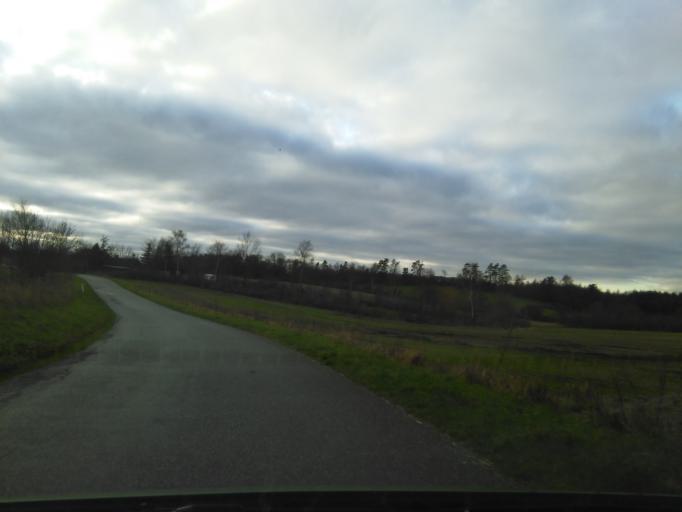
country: DK
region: Central Jutland
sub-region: Arhus Kommune
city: Sabro
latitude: 56.1768
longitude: 10.0462
